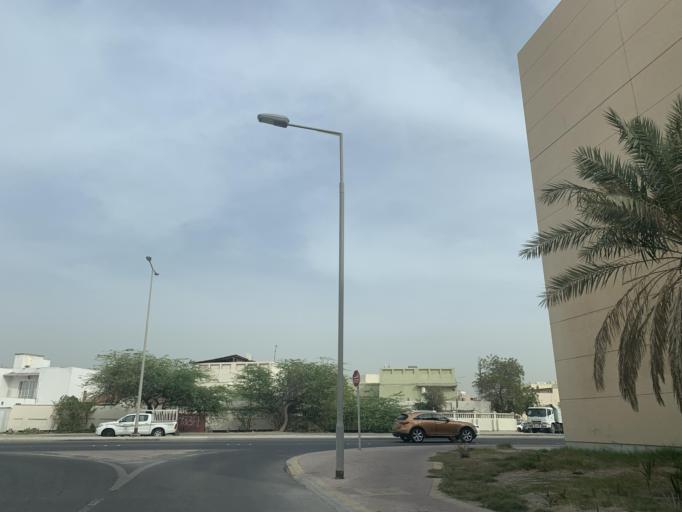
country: BH
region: Northern
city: Madinat `Isa
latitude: 26.1764
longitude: 50.5506
